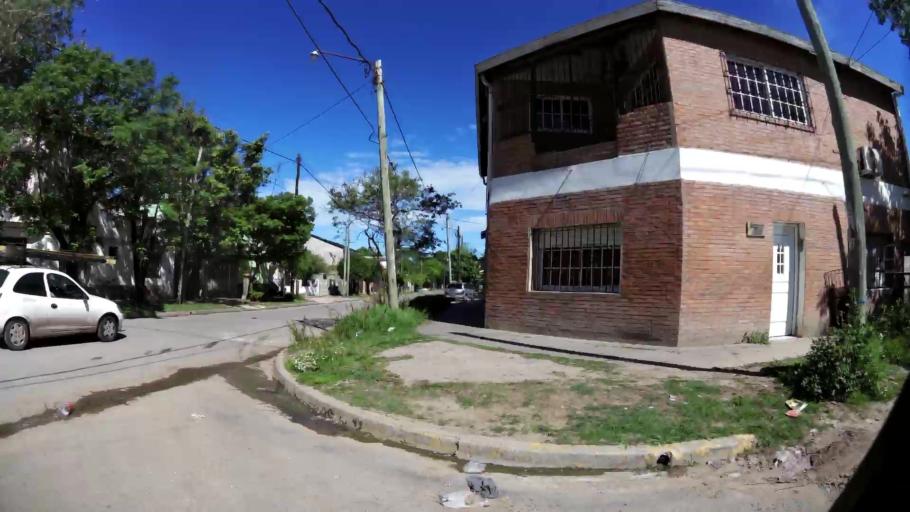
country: AR
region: Buenos Aires
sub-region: Partido de Almirante Brown
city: Adrogue
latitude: -34.7820
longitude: -58.3451
